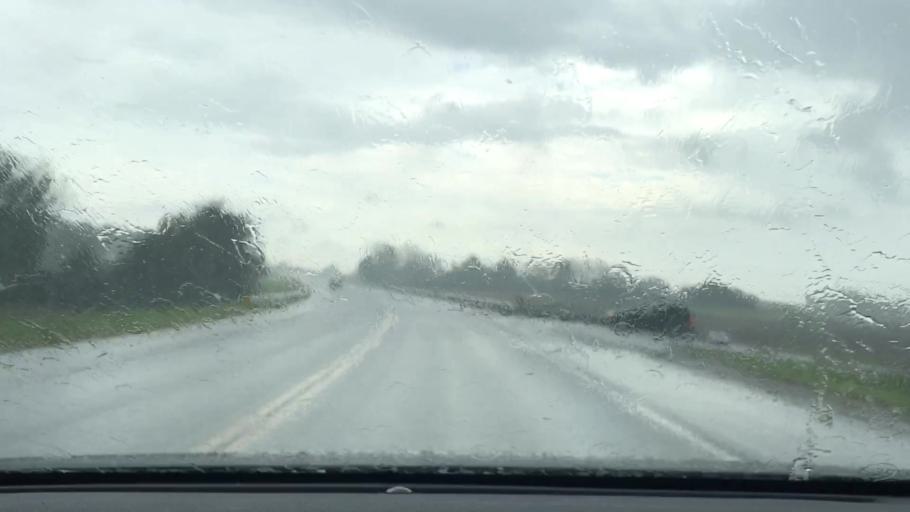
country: US
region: Tennessee
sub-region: Macon County
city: Lafayette
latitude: 36.4984
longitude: -85.9663
